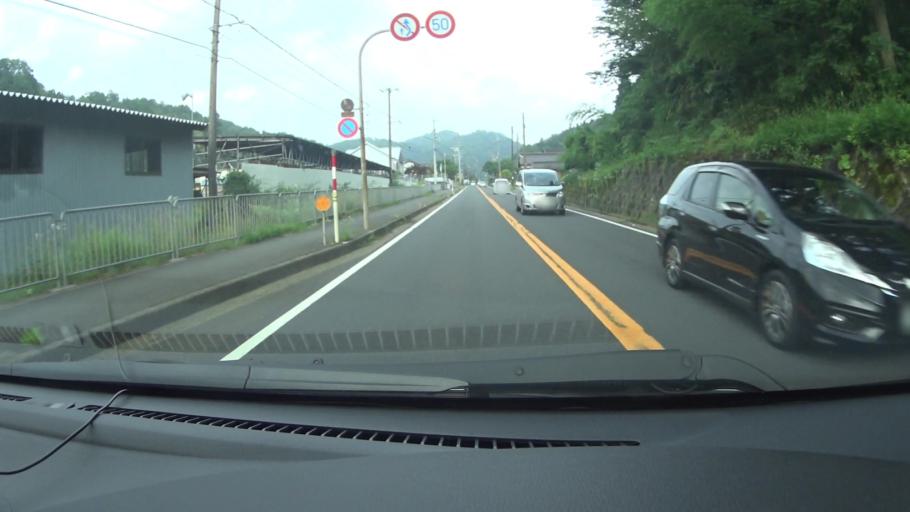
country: JP
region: Kyoto
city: Maizuru
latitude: 35.4857
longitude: 135.4556
